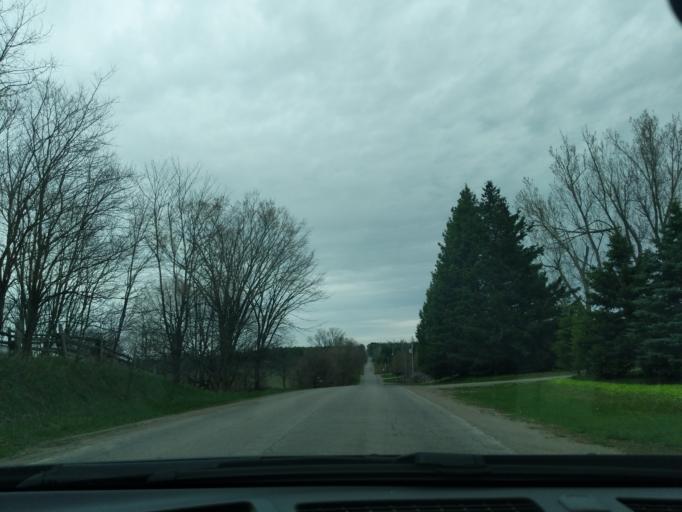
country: CA
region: Ontario
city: Orangeville
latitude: 44.0115
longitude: -79.9665
